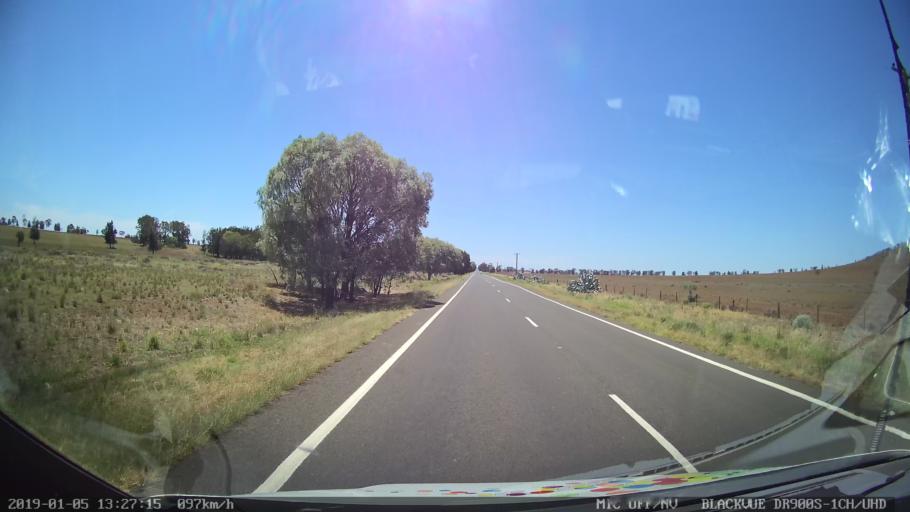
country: AU
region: New South Wales
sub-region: Gunnedah
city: Gunnedah
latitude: -31.0461
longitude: 150.0268
